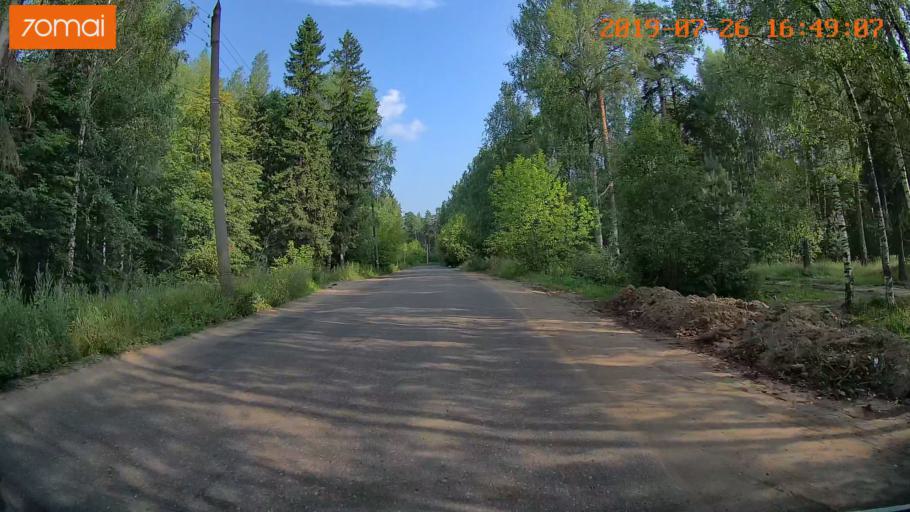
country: RU
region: Ivanovo
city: Bogorodskoye
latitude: 57.0311
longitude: 41.0190
